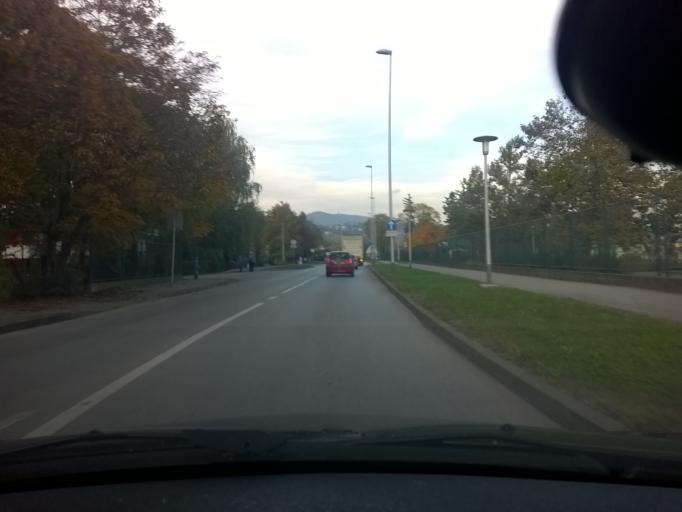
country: HR
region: Grad Zagreb
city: Stenjevec
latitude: 45.8102
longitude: 15.8787
